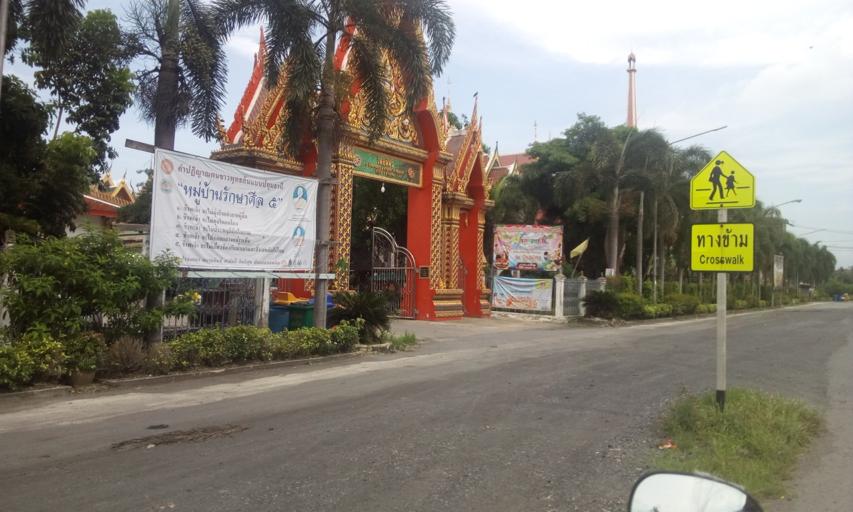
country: TH
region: Pathum Thani
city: Ban Lam Luk Ka
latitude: 14.0197
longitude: 100.8435
